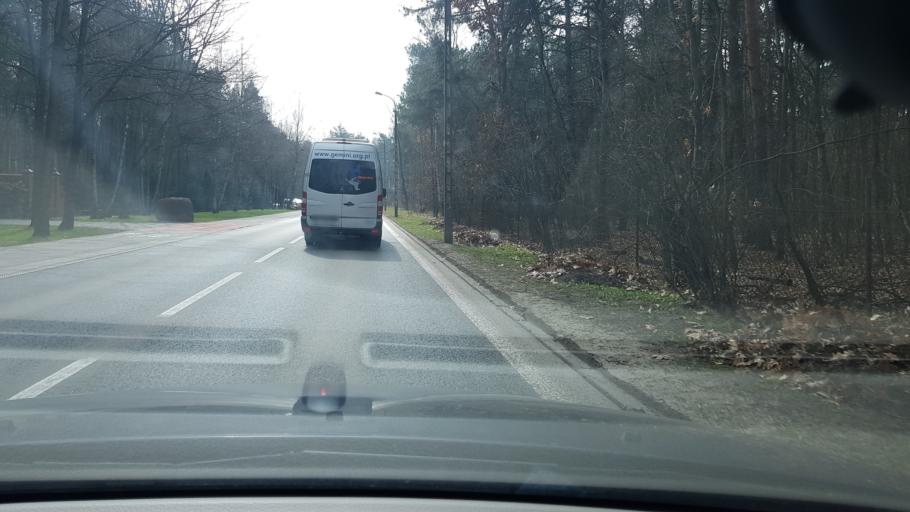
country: PL
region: Masovian Voivodeship
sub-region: Warszawa
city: Wesola
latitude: 52.2381
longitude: 21.2222
